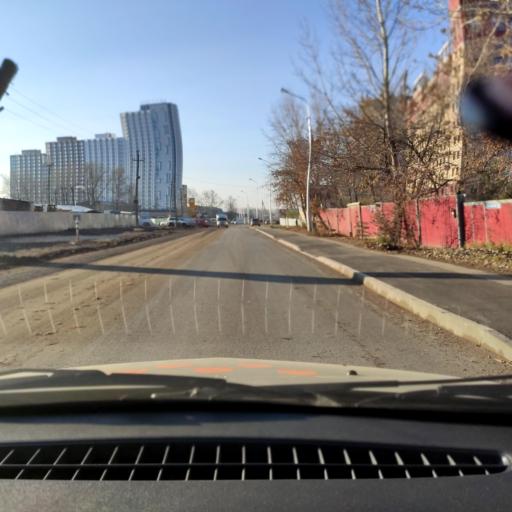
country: RU
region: Bashkortostan
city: Ufa
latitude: 54.6863
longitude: 55.9865
